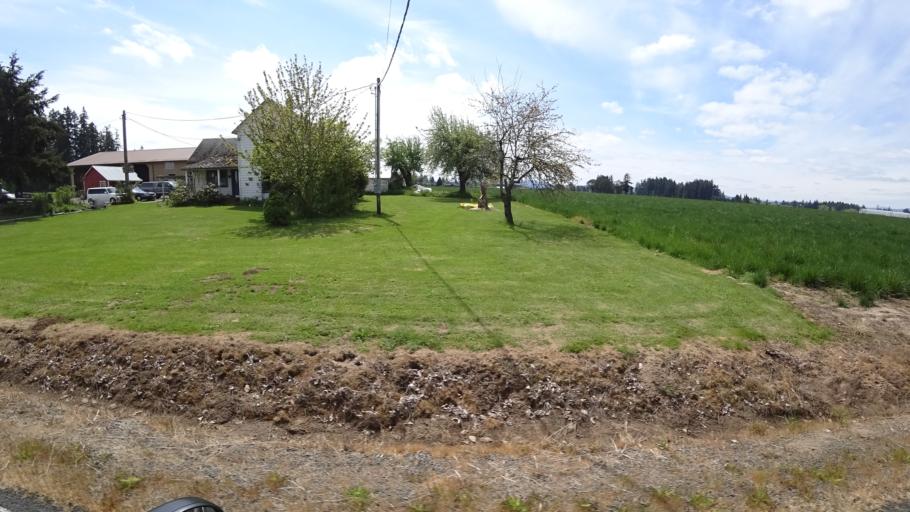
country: US
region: Oregon
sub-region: Washington County
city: Hillsboro
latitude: 45.5438
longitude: -123.0104
